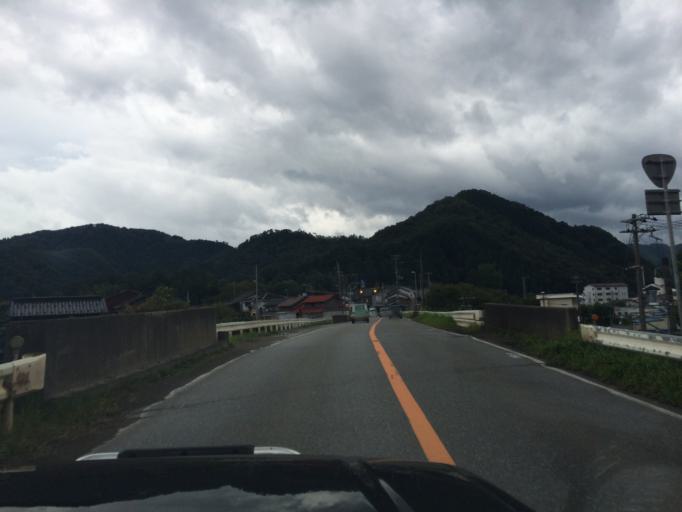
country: JP
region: Hyogo
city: Toyooka
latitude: 35.4066
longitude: 134.7778
